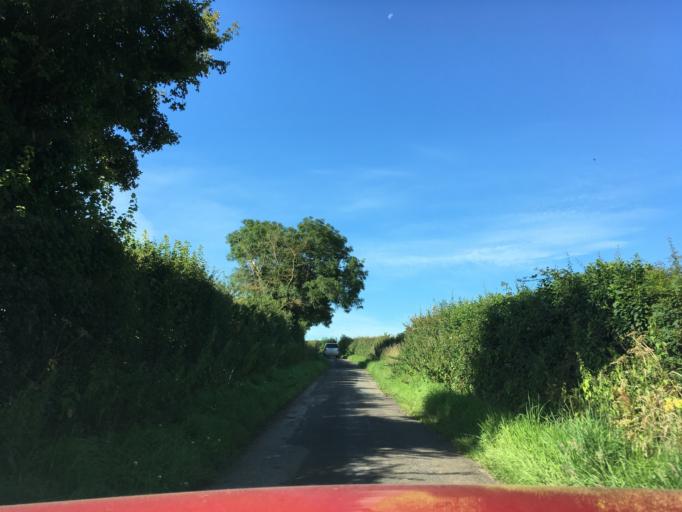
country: GB
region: England
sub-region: Bath and North East Somerset
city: Publow
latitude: 51.3991
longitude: -2.5309
